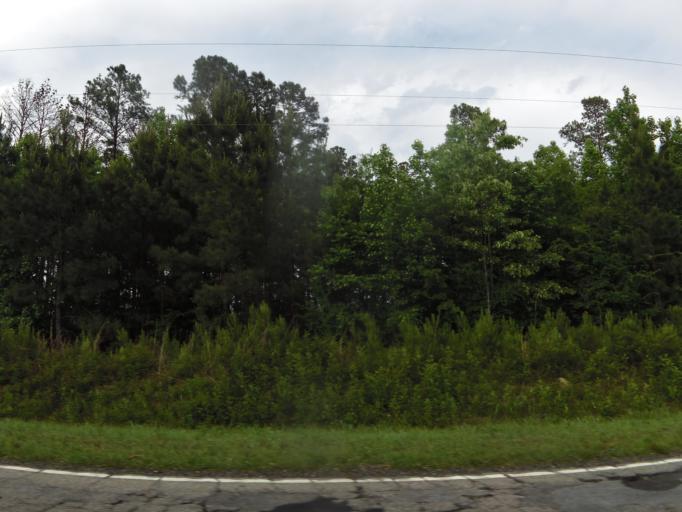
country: US
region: South Carolina
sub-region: Jasper County
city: Ridgeland
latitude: 32.4897
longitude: -81.1232
